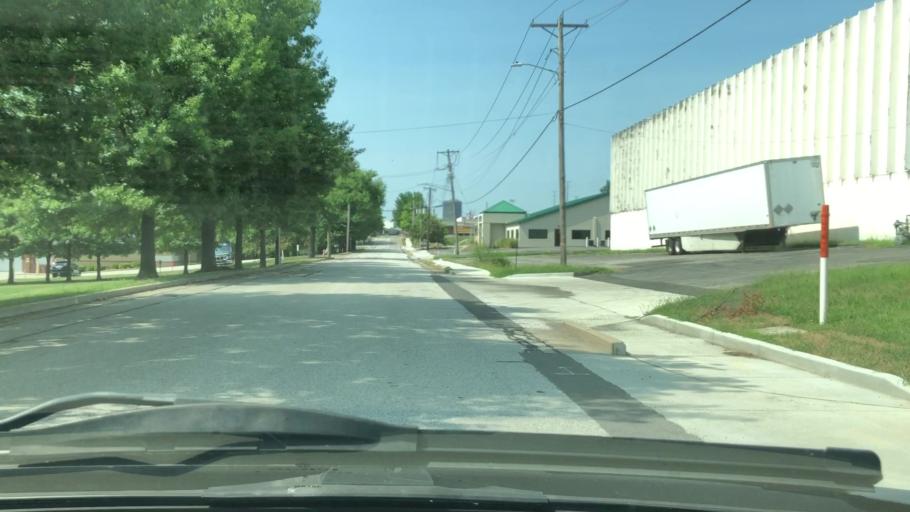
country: US
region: Missouri
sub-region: Saint Louis County
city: Maplewood
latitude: 38.6193
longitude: -90.3359
